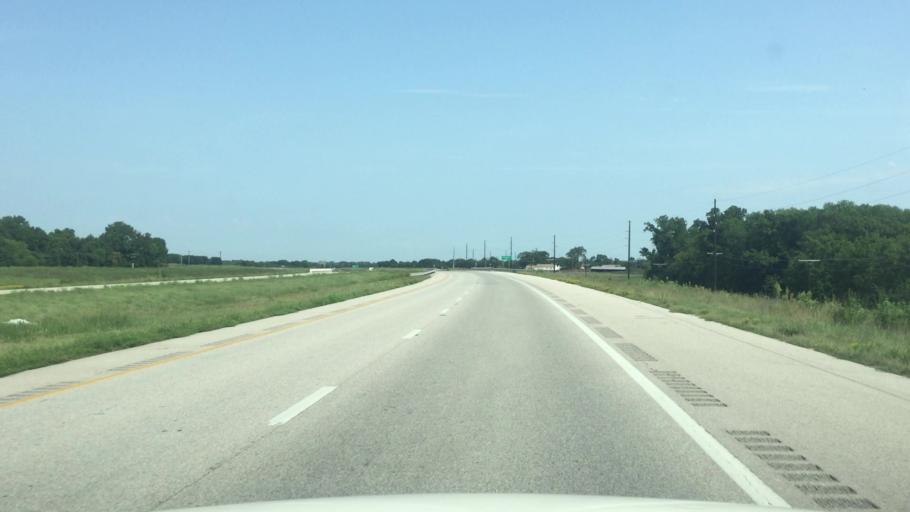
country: US
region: Kansas
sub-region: Montgomery County
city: Coffeyville
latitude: 37.0650
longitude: -95.5830
